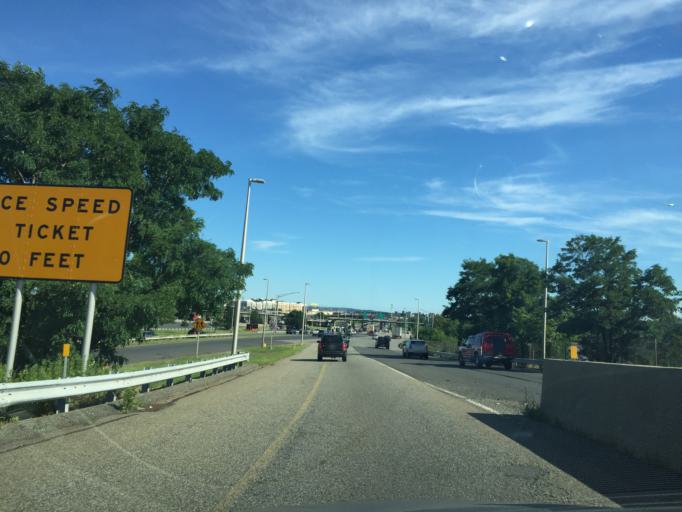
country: US
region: New Jersey
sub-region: Union County
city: Elizabeth
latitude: 40.6713
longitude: -74.1864
